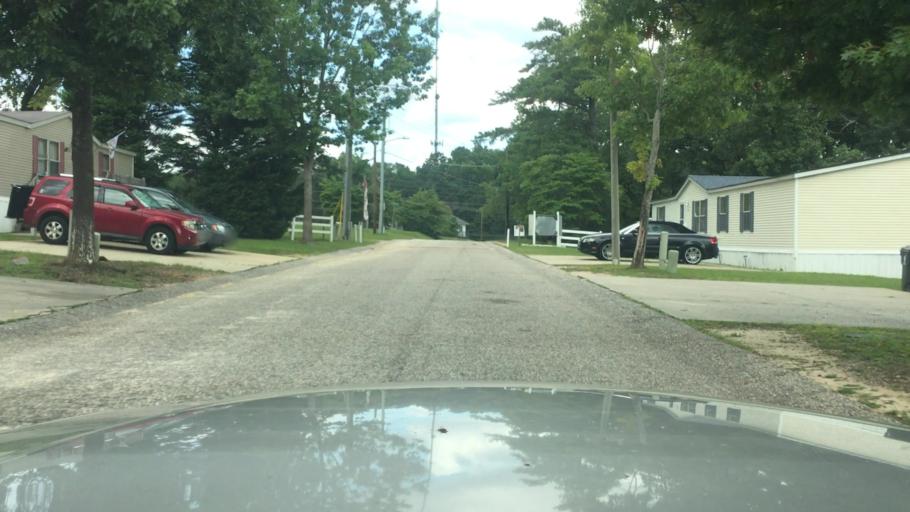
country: US
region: North Carolina
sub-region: Cumberland County
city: Hope Mills
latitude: 35.0423
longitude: -78.9802
